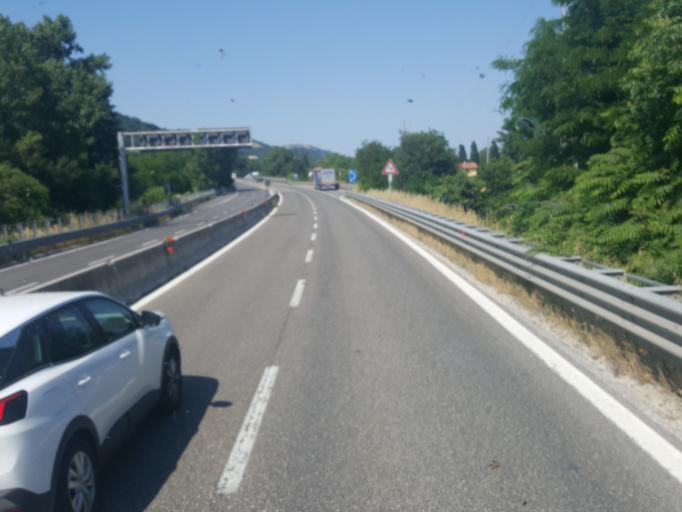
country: IT
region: The Marches
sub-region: Provincia di Ancona
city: Serra San Quirico
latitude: 43.4422
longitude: 13.0303
